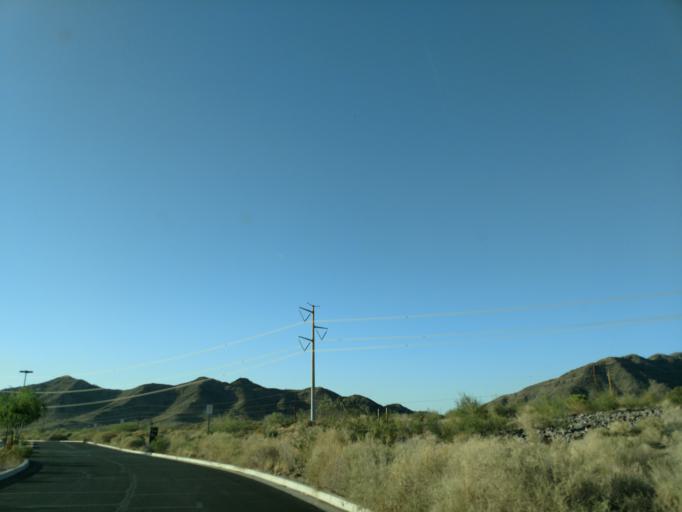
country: US
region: Arizona
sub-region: Maricopa County
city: Laveen
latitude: 33.3093
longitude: -112.1544
